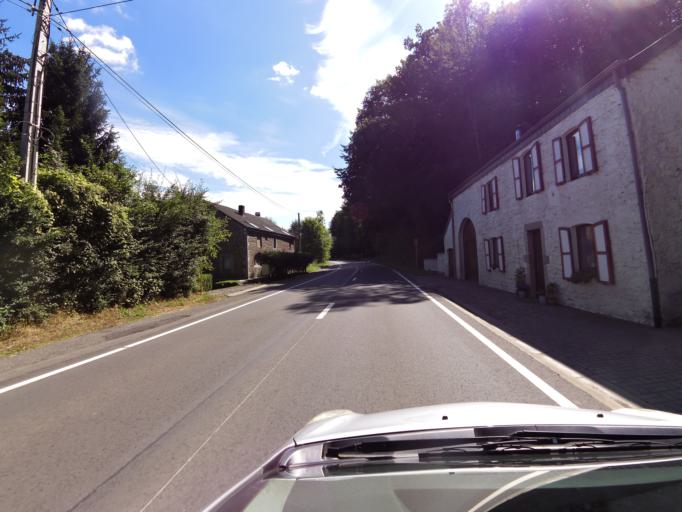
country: BE
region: Wallonia
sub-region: Province du Luxembourg
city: Rendeux
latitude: 50.2519
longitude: 5.4868
